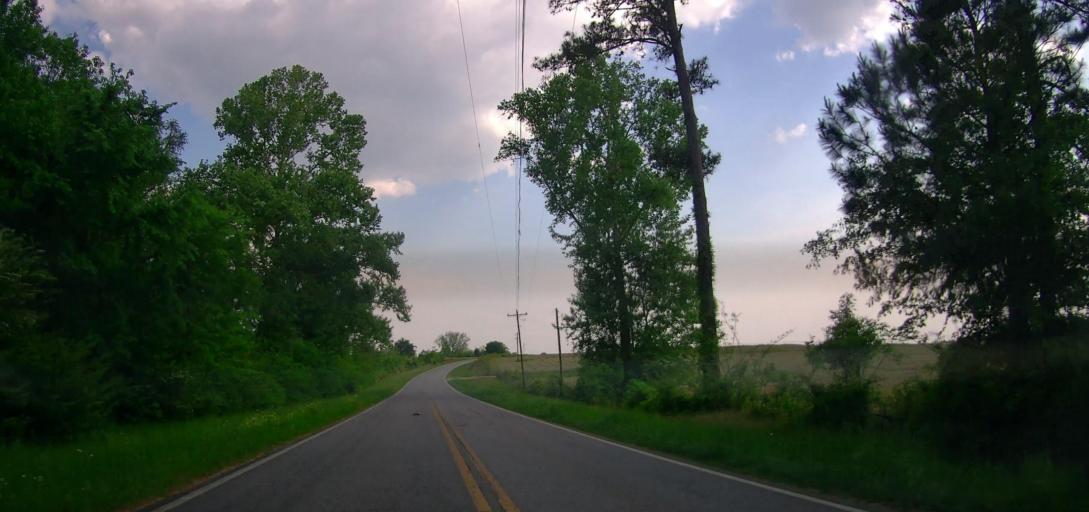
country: US
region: Georgia
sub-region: Laurens County
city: East Dublin
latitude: 32.6132
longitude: -82.8692
